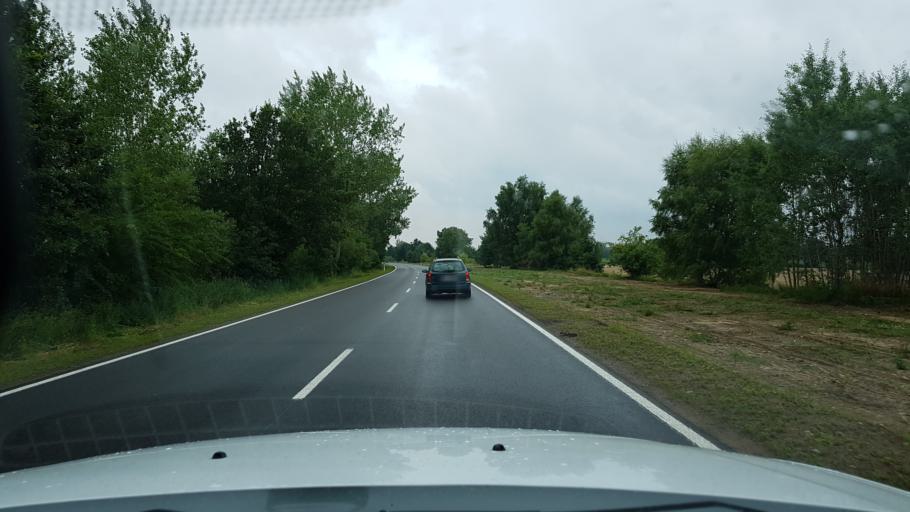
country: PL
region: West Pomeranian Voivodeship
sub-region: Powiat goleniowski
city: Maszewo
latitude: 53.4339
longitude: 15.0685
